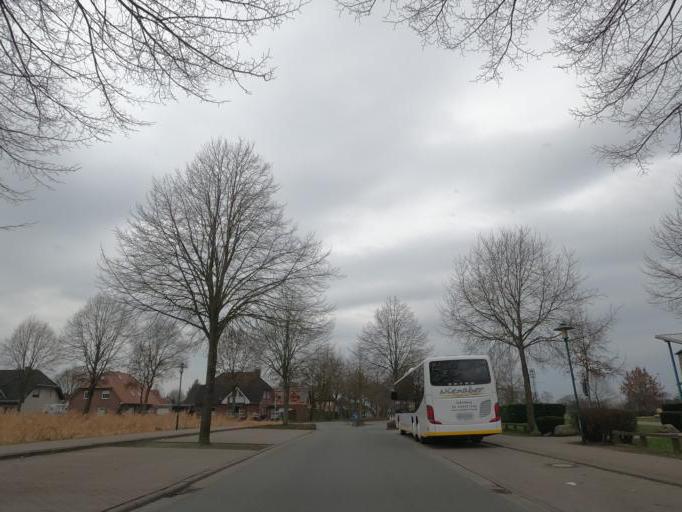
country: DE
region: Lower Saxony
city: Molbergen
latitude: 52.8631
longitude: 7.9216
